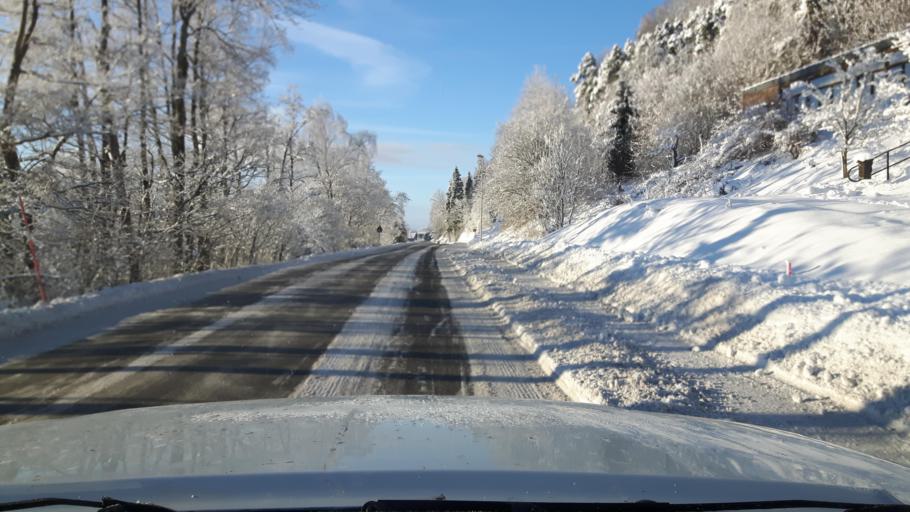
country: SE
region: Halland
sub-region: Kungsbacka Kommun
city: Fjaeras kyrkby
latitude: 57.5486
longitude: 12.1812
